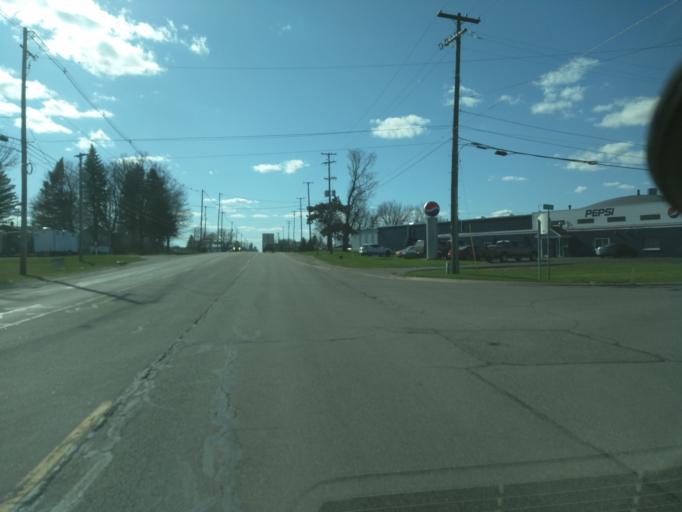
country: US
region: Michigan
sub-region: Eaton County
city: Waverly
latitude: 42.7753
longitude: -84.6201
